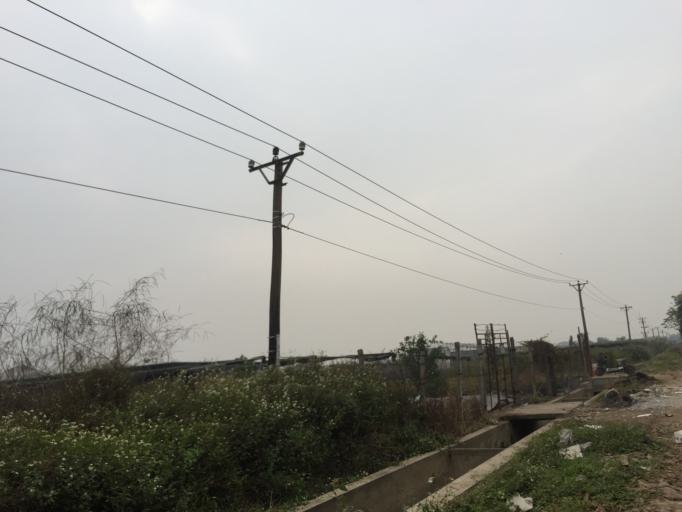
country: VN
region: Hung Yen
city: Van Giang
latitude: 20.9680
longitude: 105.9114
